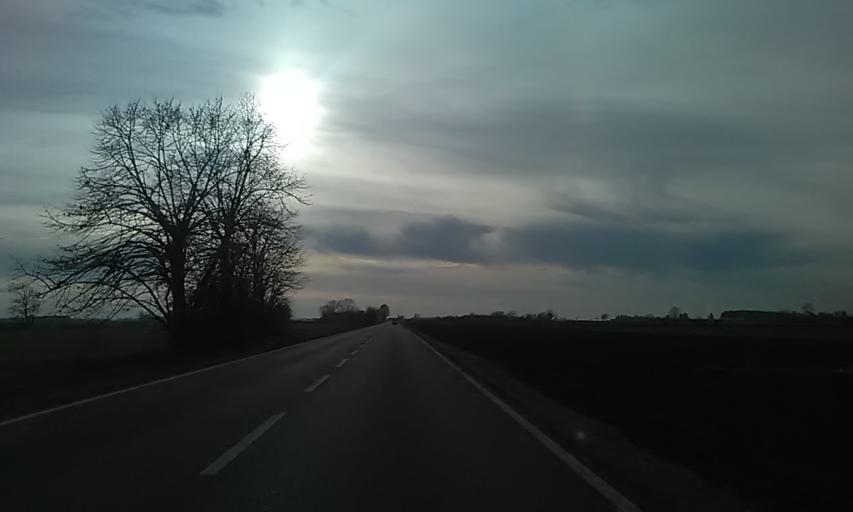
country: IT
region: Piedmont
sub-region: Provincia di Torino
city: Villareggia
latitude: 45.2907
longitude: 7.9981
